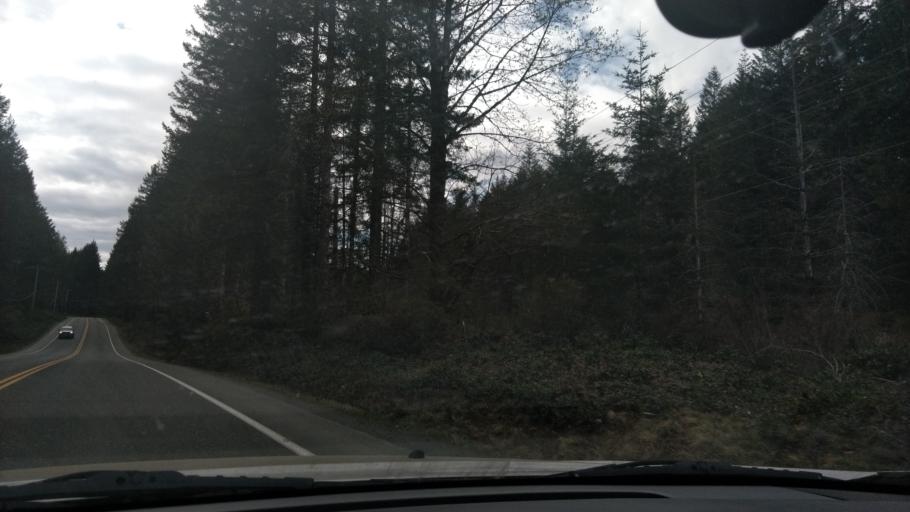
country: CA
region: British Columbia
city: Campbell River
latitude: 50.0292
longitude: -125.3464
